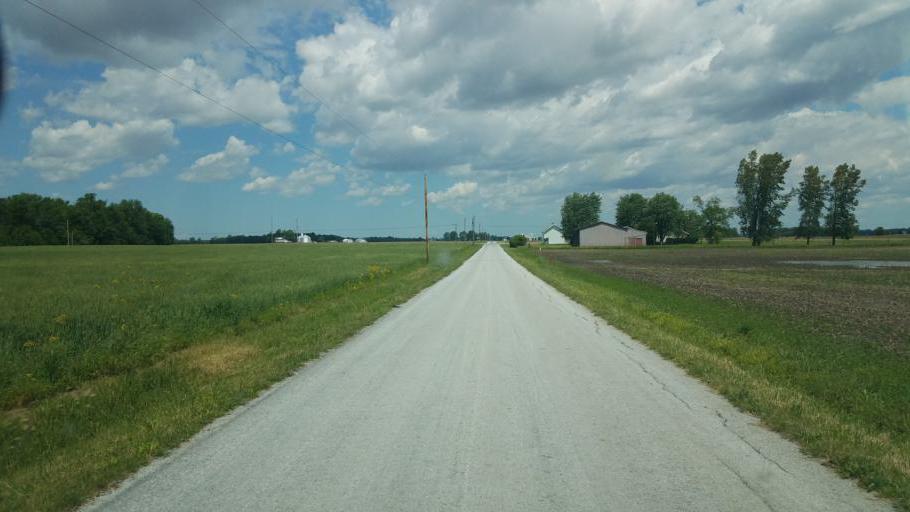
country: US
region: Ohio
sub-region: Hardin County
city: Forest
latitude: 40.6846
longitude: -83.4777
